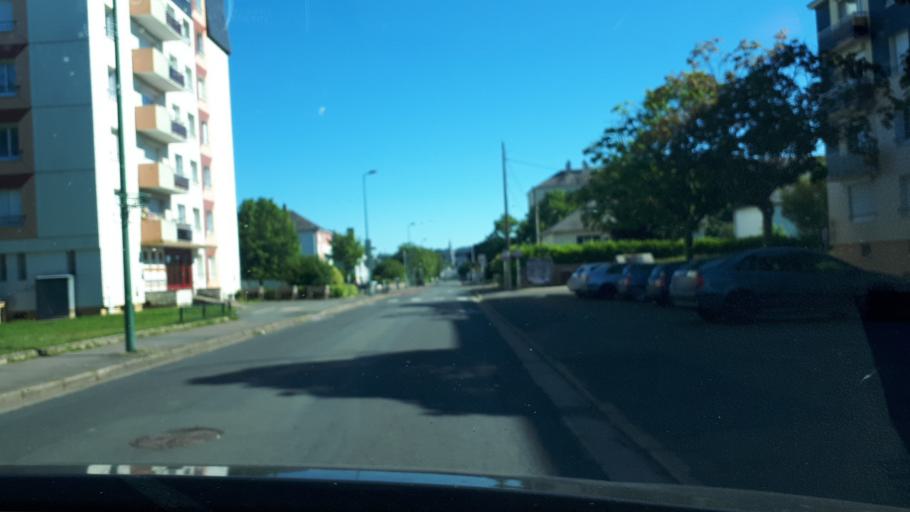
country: FR
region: Centre
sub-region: Departement du Loir-et-Cher
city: Vendome
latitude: 47.8063
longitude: 1.0659
